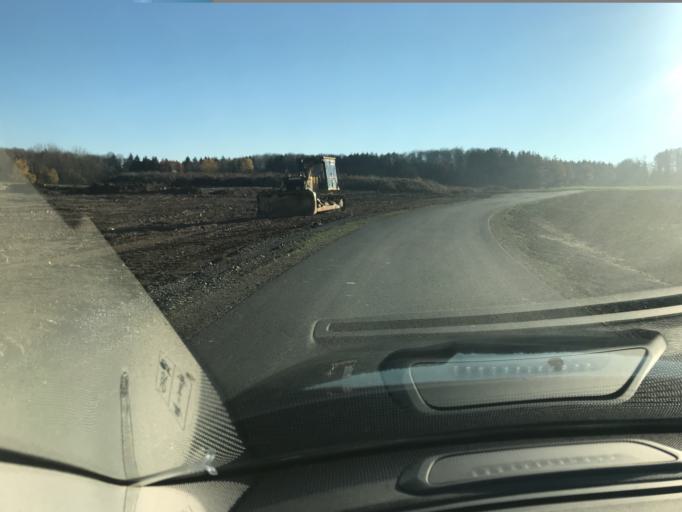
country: DE
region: Rheinland-Pfalz
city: Girod
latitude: 50.4435
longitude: 7.9279
